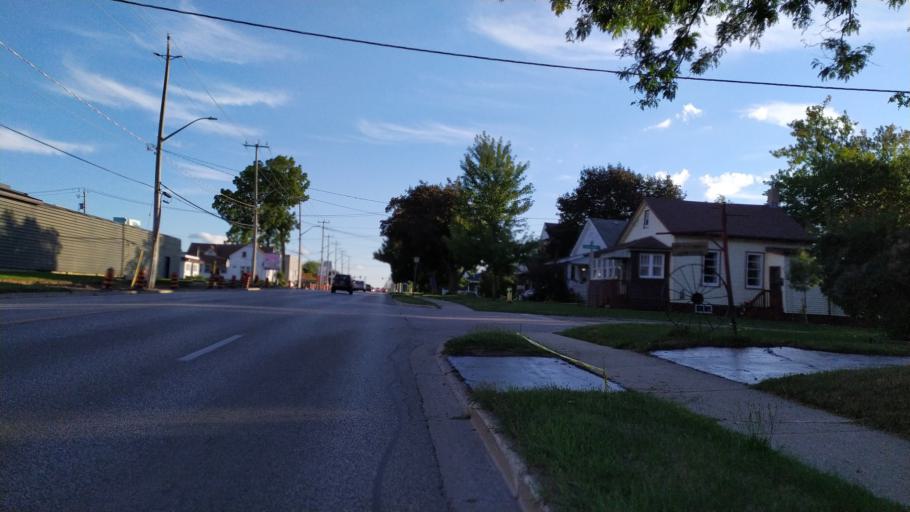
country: CA
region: Ontario
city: Stratford
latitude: 43.3583
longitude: -80.9940
